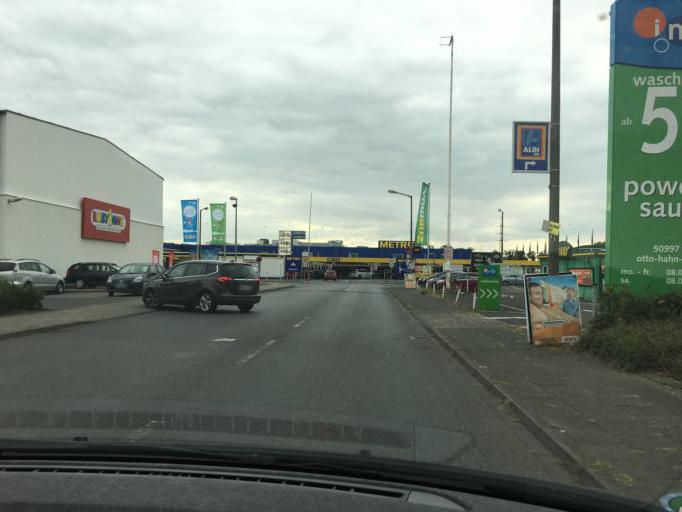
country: DE
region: North Rhine-Westphalia
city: Wesseling
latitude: 50.8582
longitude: 6.9731
